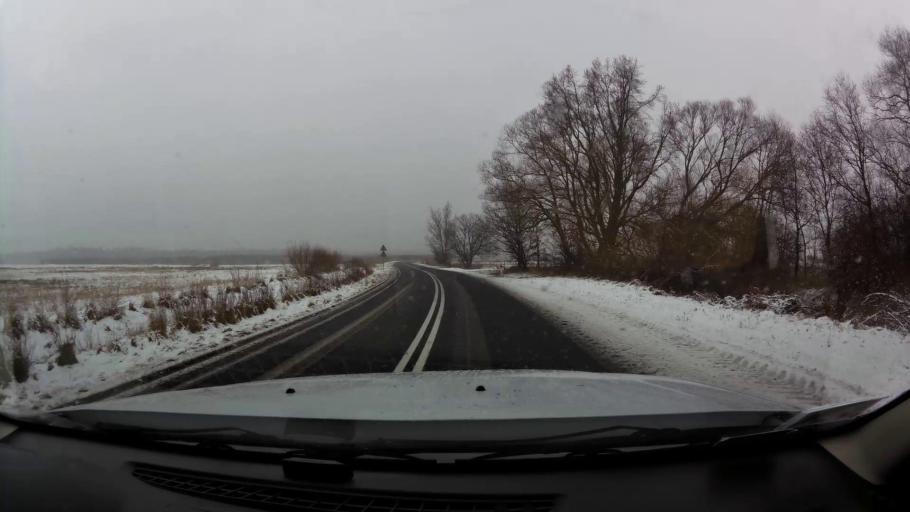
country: PL
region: West Pomeranian Voivodeship
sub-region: Powiat gryficki
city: Mrzezyno
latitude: 54.1082
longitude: 15.2673
